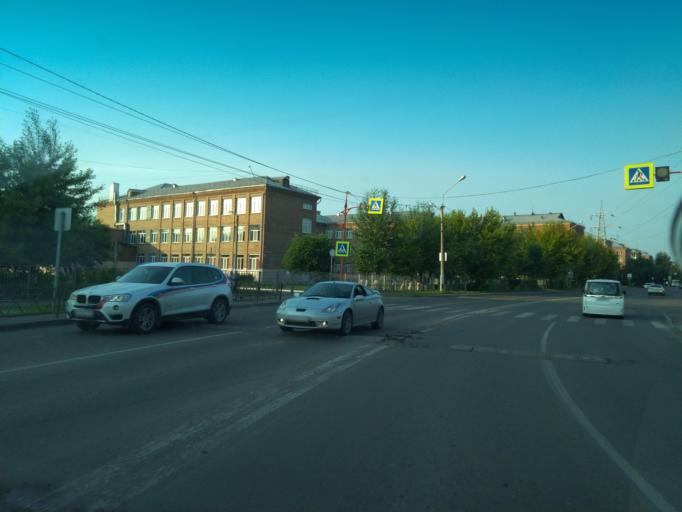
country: RU
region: Krasnoyarskiy
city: Krasnoyarsk
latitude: 56.0026
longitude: 92.9501
